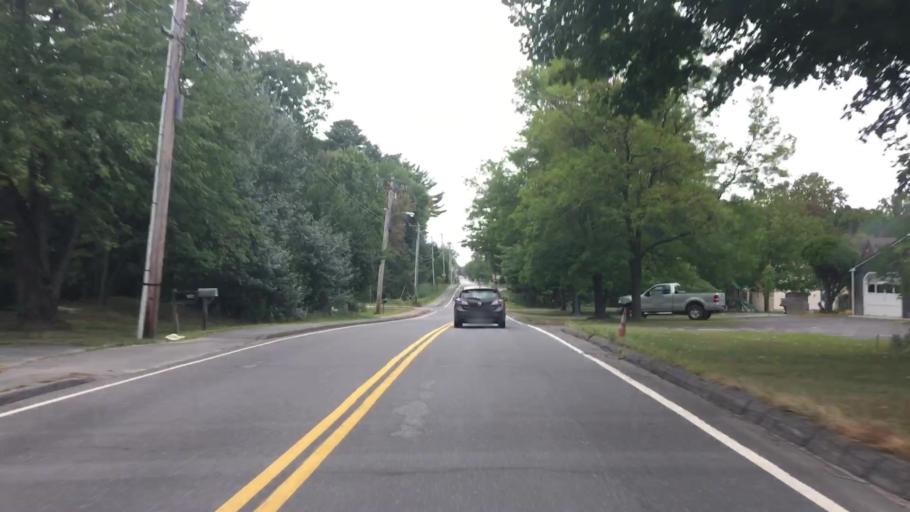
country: US
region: Maine
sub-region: Cumberland County
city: Yarmouth
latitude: 43.8157
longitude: -70.1826
